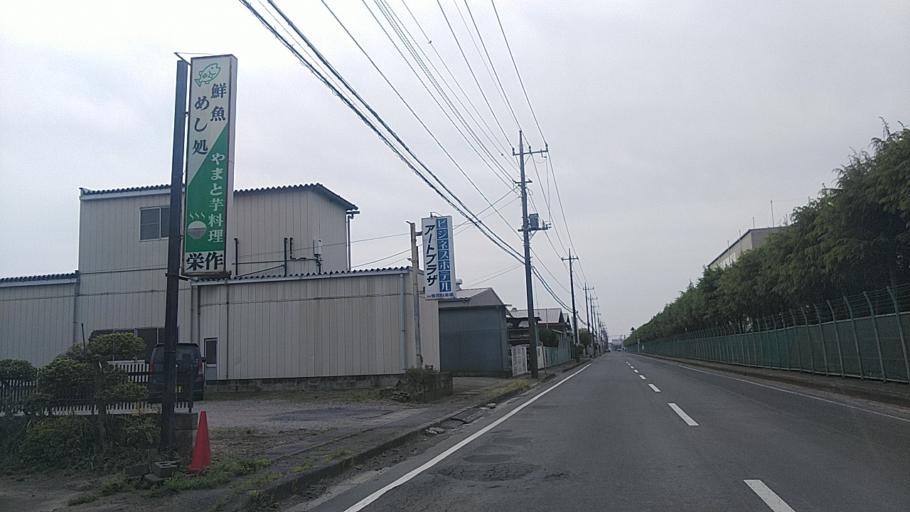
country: JP
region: Gunma
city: Ota
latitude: 36.2753
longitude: 139.3419
